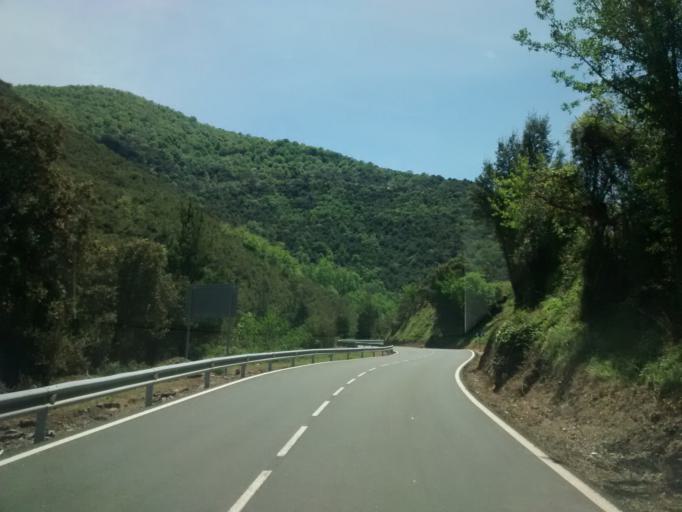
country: ES
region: Cantabria
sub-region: Provincia de Cantabria
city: Potes
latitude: 43.1067
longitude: -4.6413
